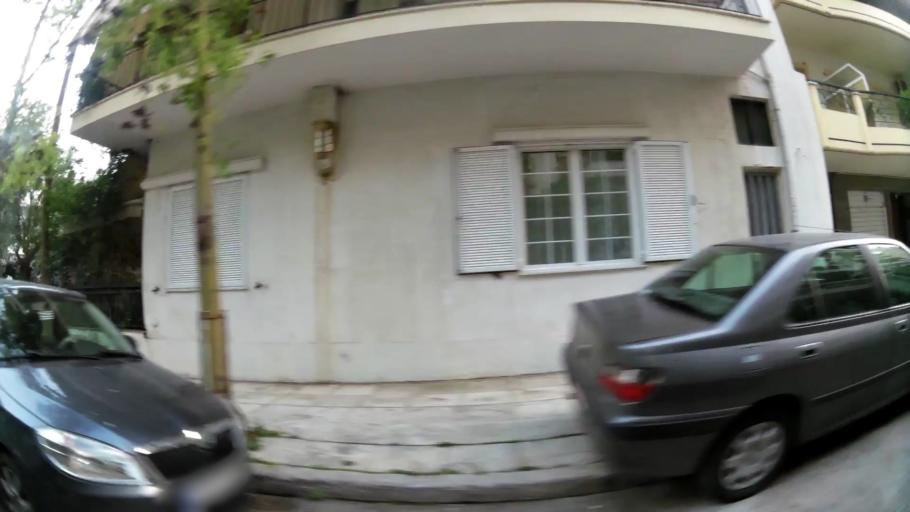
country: GR
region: Attica
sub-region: Nomos Piraios
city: Nikaia
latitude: 37.9718
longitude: 23.6500
